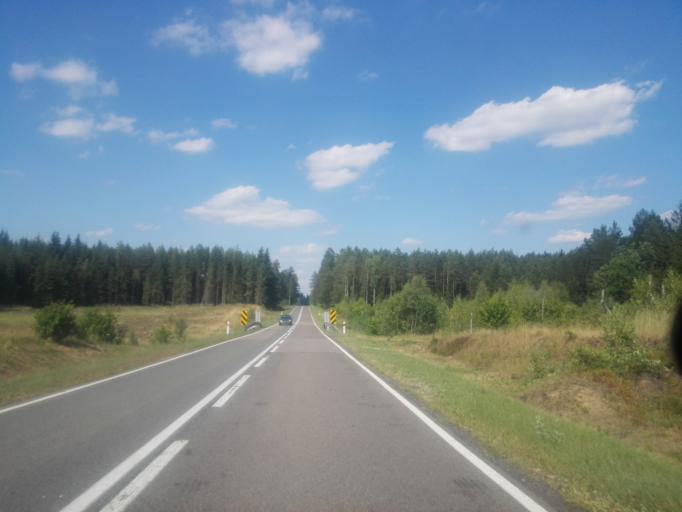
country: PL
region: Podlasie
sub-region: Powiat sejnenski
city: Sejny
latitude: 53.9991
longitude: 23.3139
